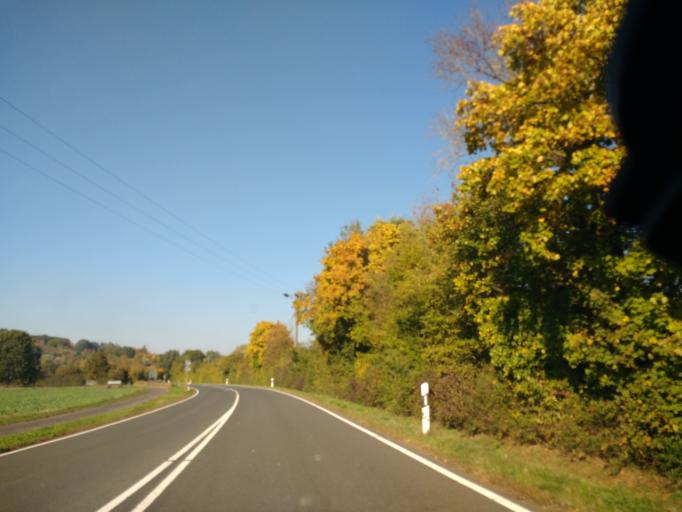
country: DE
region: Rheinland-Pfalz
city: Kanzem
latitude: 49.6670
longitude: 6.5605
